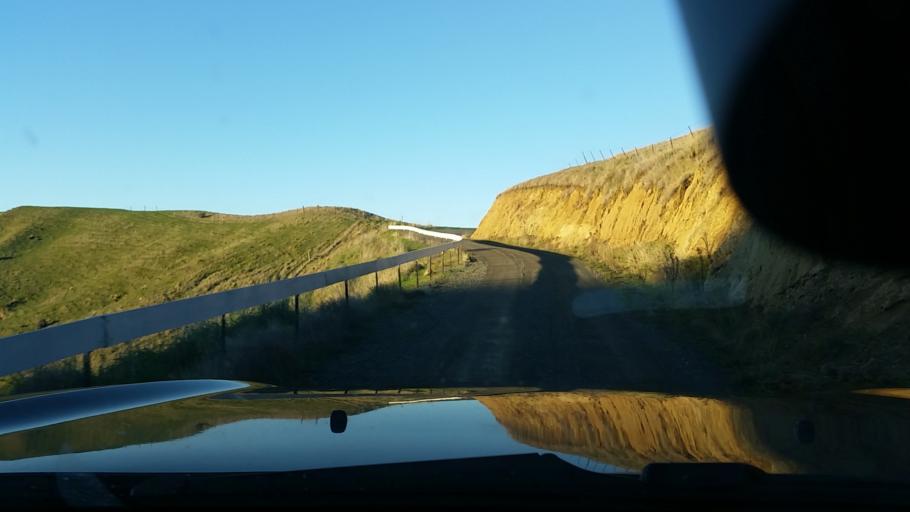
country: NZ
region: Marlborough
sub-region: Marlborough District
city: Blenheim
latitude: -41.7484
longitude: 174.0572
